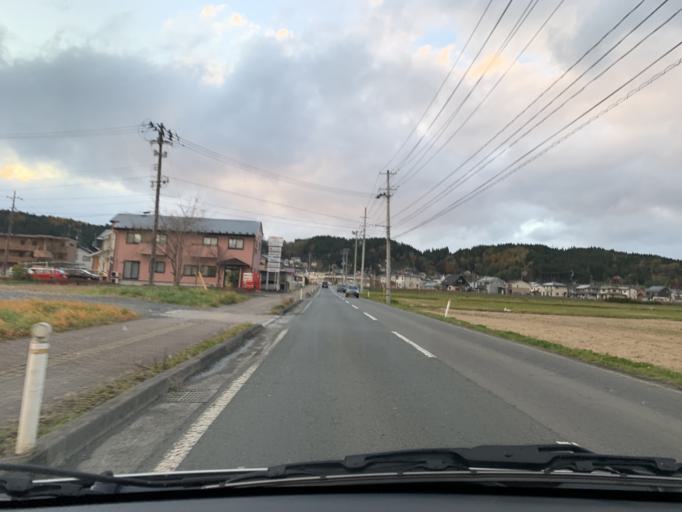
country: JP
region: Iwate
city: Mizusawa
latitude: 39.0541
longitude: 141.1291
